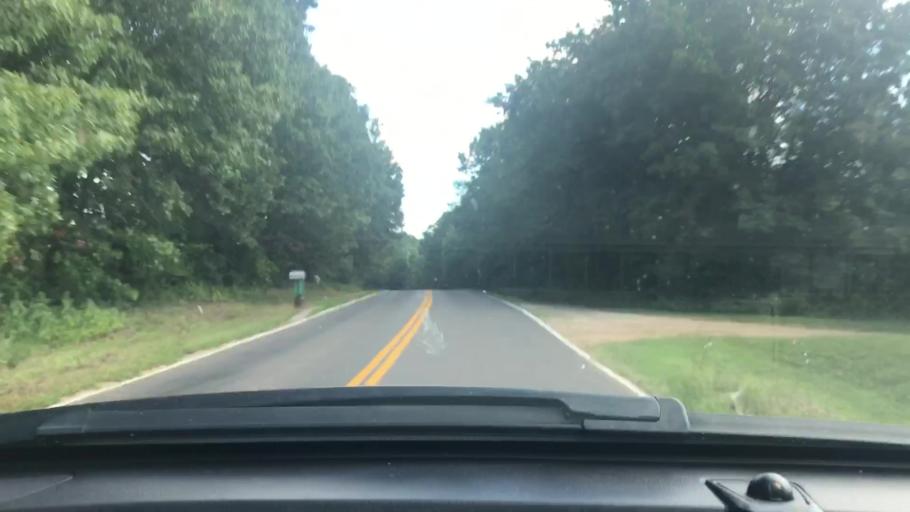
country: US
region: Missouri
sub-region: Wright County
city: Hartville
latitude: 37.3556
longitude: -92.3414
